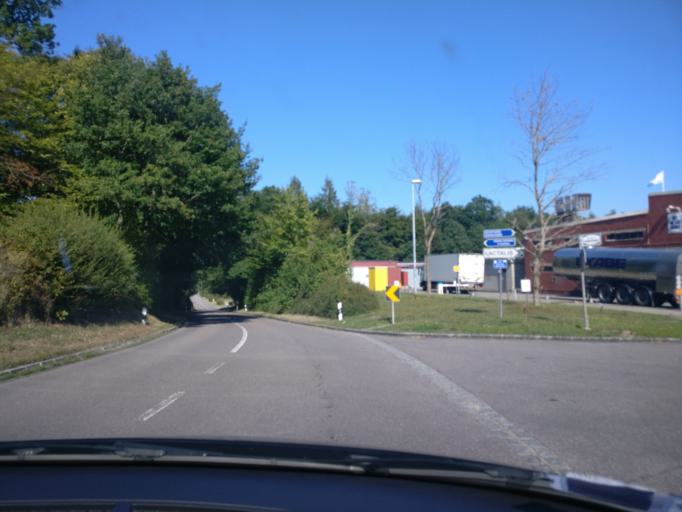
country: LU
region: Grevenmacher
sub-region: Canton de Grevenmacher
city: Junglinster
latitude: 49.7149
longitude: 6.3025
